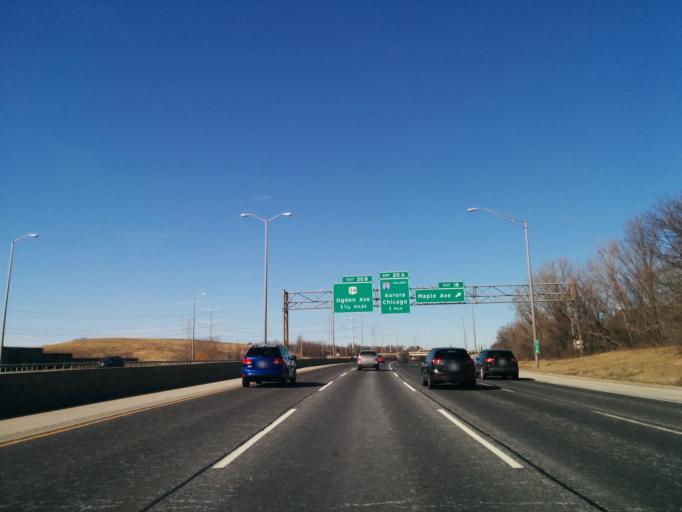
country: US
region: Illinois
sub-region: DuPage County
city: Lisle
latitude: 41.7807
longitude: -88.0535
